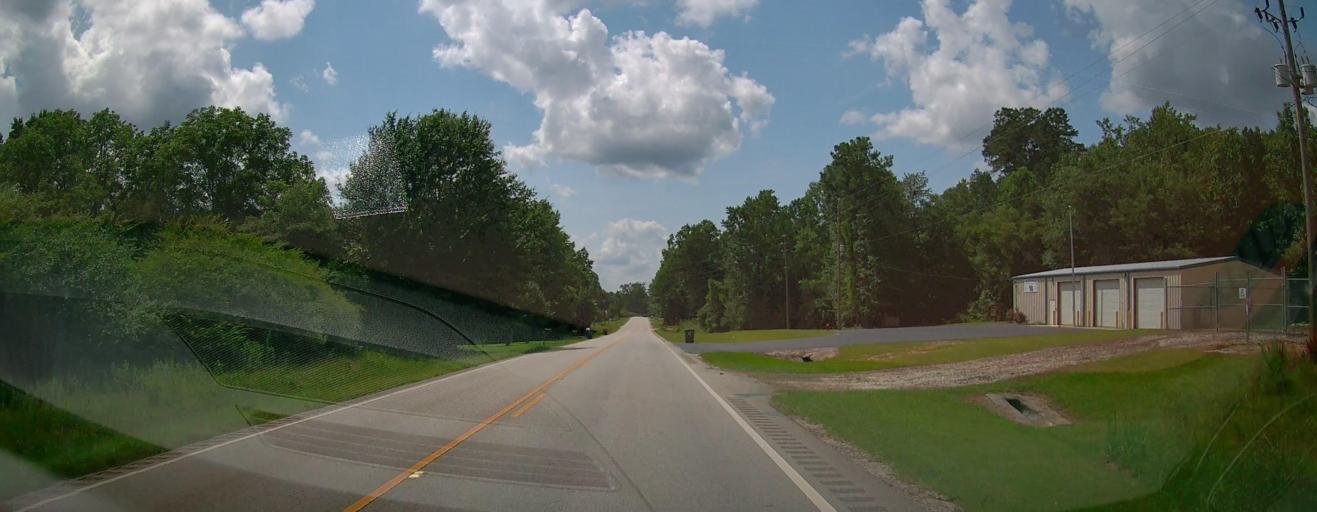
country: US
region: Alabama
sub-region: Cleburne County
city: Heflin
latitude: 33.5747
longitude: -85.4537
